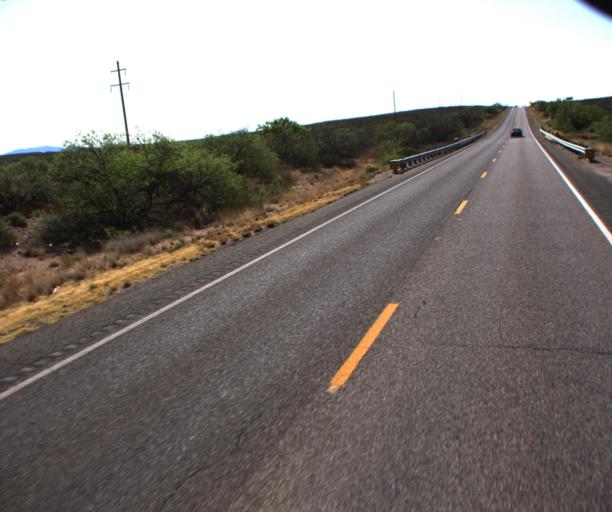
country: US
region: Arizona
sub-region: Cochise County
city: Tombstone
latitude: 31.7552
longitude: -110.1050
